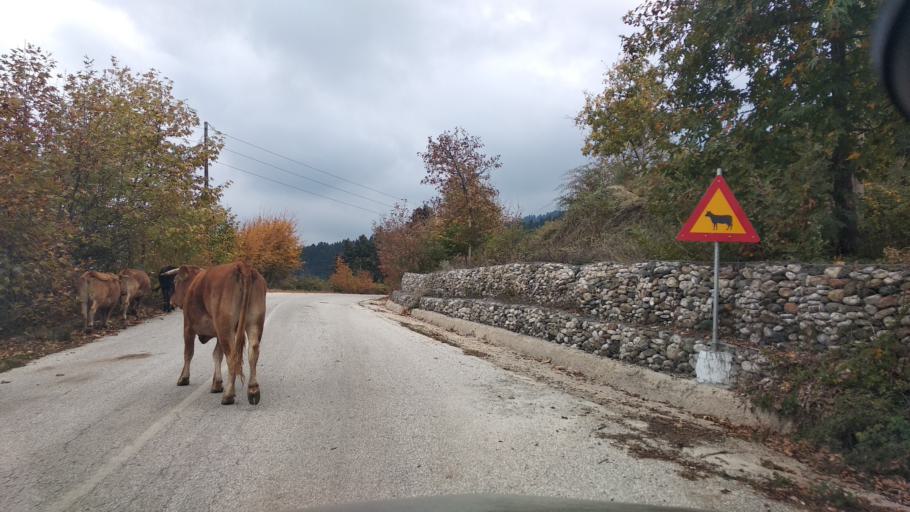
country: GR
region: Thessaly
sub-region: Trikala
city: Kalampaka
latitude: 39.5921
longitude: 21.4943
